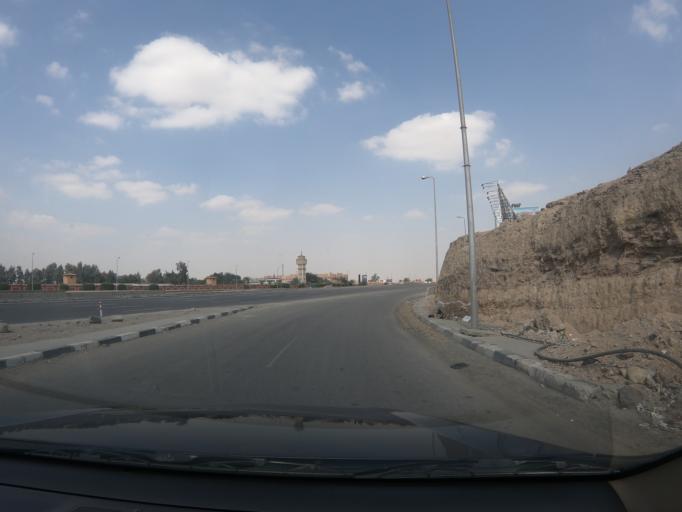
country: EG
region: Muhafazat al Qalyubiyah
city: Al Khankah
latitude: 30.0829
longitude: 31.4717
